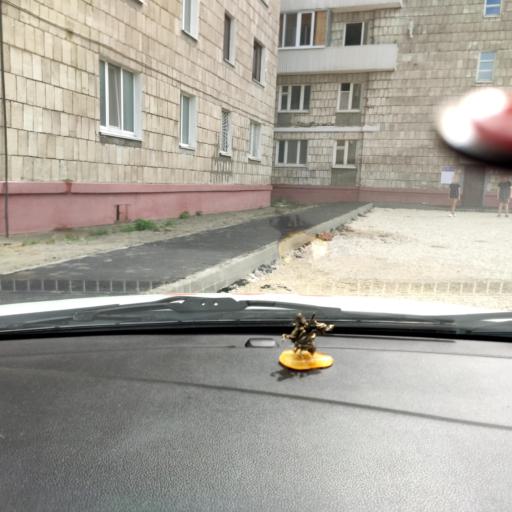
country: RU
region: Tatarstan
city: Staroye Arakchino
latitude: 55.8073
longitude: 48.9202
